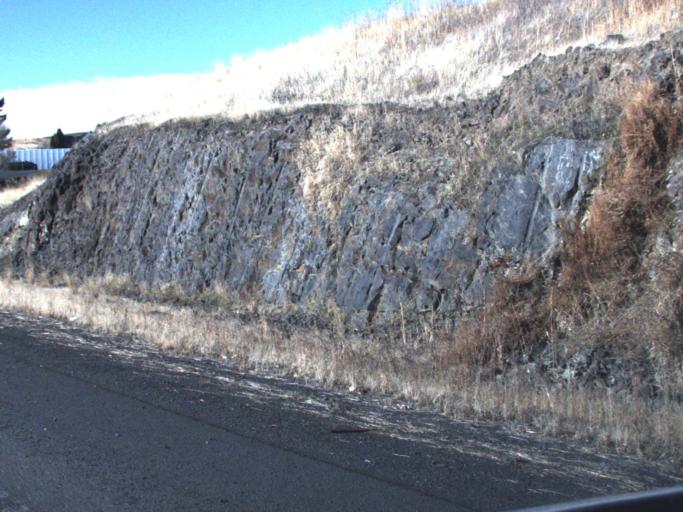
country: US
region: Washington
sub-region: Whitman County
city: Pullman
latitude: 46.7308
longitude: -117.0911
